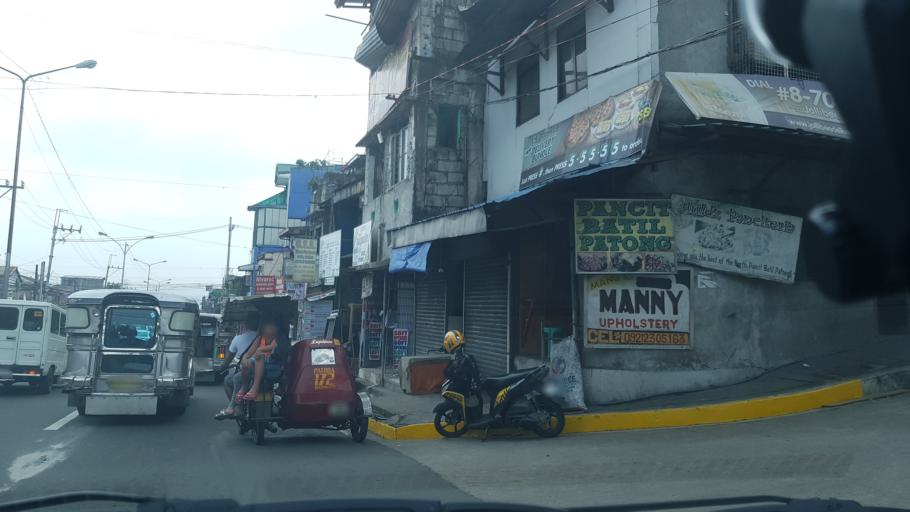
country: PH
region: Calabarzon
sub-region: Province of Rizal
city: San Mateo
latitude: 14.6907
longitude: 121.0966
